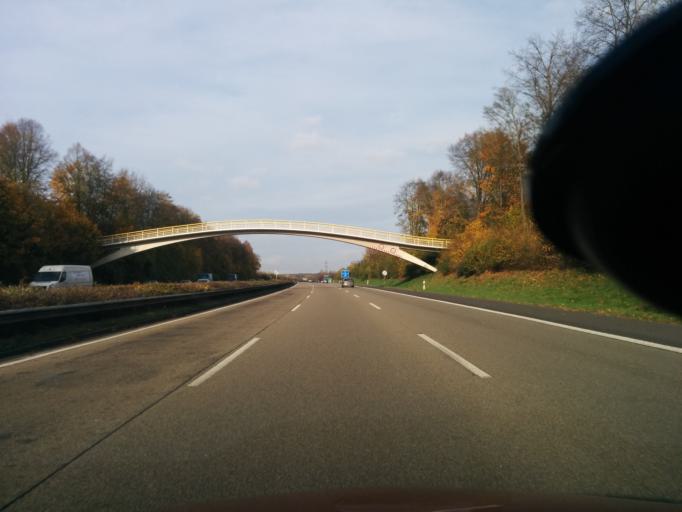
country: DE
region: Rheinland-Pfalz
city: Weitersburg
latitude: 50.4116
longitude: 7.6092
